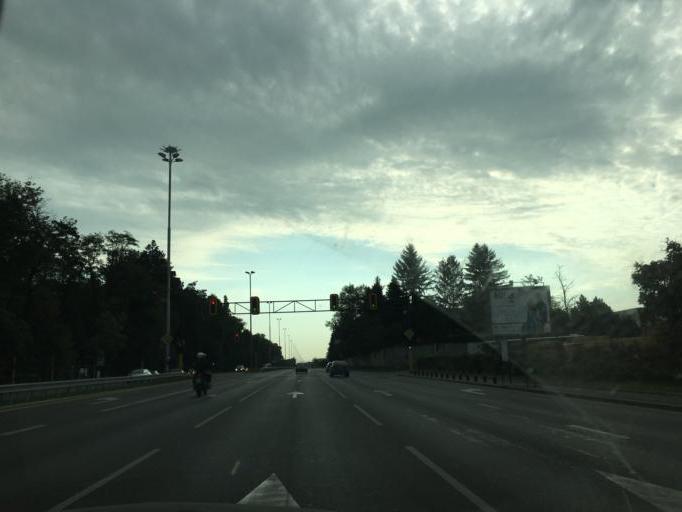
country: BG
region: Sofia-Capital
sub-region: Stolichna Obshtina
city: Sofia
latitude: 42.6360
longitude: 23.4264
